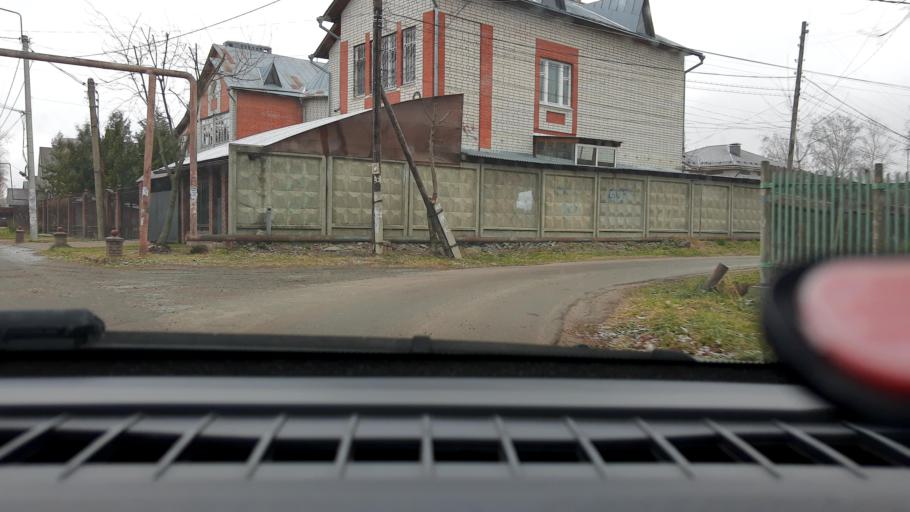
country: RU
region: Nizjnij Novgorod
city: Burevestnik
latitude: 56.2034
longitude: 43.7988
